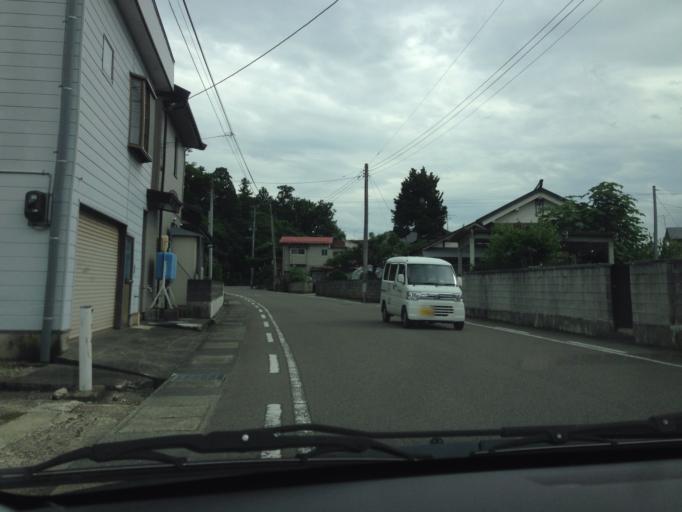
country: JP
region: Fukushima
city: Kitakata
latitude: 37.4585
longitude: 139.8400
